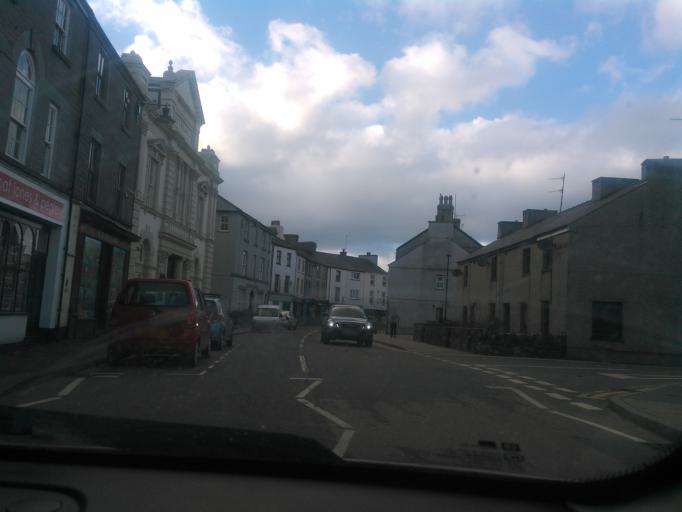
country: GB
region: Wales
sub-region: Gwynedd
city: Bethesda
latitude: 53.1796
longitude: -4.0609
